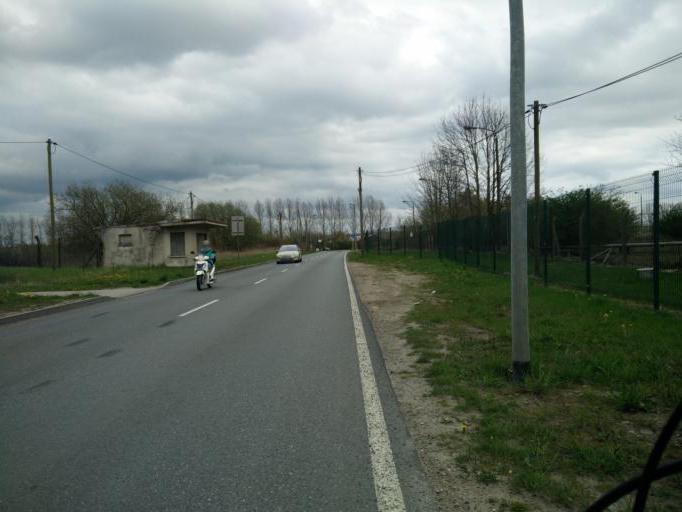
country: DE
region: Mecklenburg-Vorpommern
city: Nienhagen
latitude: 54.1425
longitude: 12.1629
